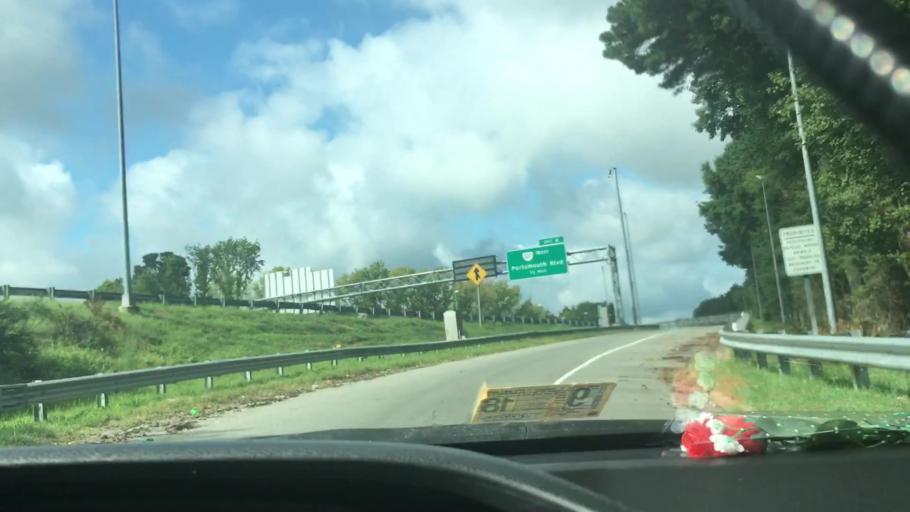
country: US
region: Virginia
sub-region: City of Portsmouth
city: Portsmouth Heights
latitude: 36.8218
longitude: -76.3371
